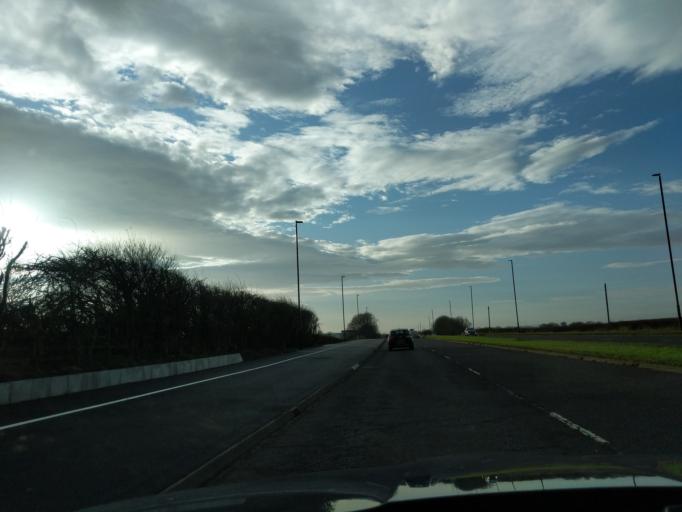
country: GB
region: England
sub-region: Newcastle upon Tyne
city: Gosforth
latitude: 55.0227
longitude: -1.5945
